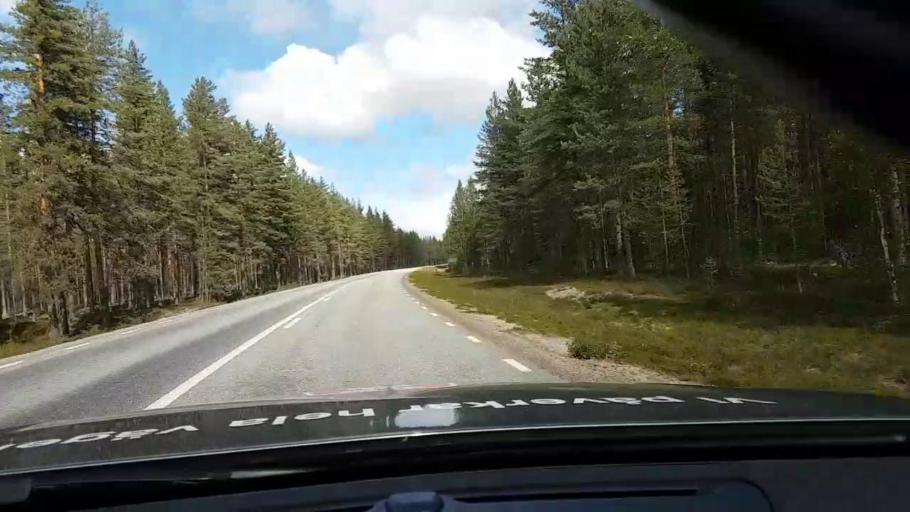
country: SE
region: Vaesternorrland
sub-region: OErnskoeldsviks Kommun
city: Bredbyn
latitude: 63.6095
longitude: 17.9000
